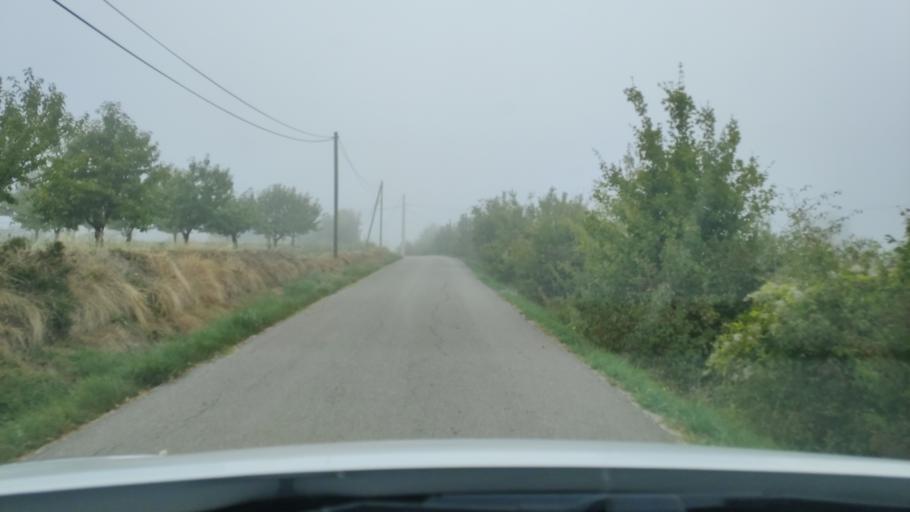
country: FR
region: Provence-Alpes-Cote d'Azur
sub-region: Departement du Vaucluse
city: Bonnieux
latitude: 43.8439
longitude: 5.3204
